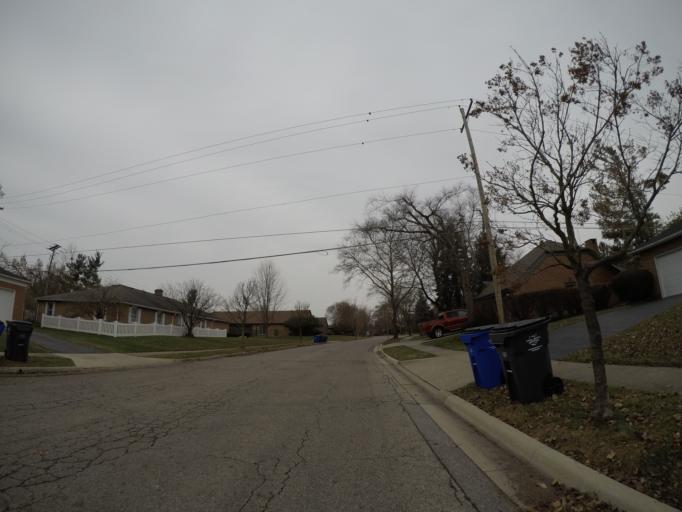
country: US
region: Ohio
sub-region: Franklin County
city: Upper Arlington
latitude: 40.0524
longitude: -83.0746
